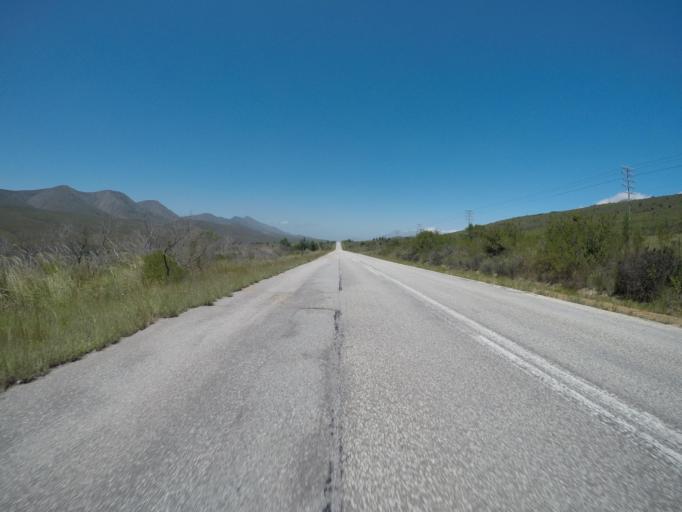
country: ZA
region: Eastern Cape
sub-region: Cacadu District Municipality
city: Kareedouw
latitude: -33.8880
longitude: 24.0906
